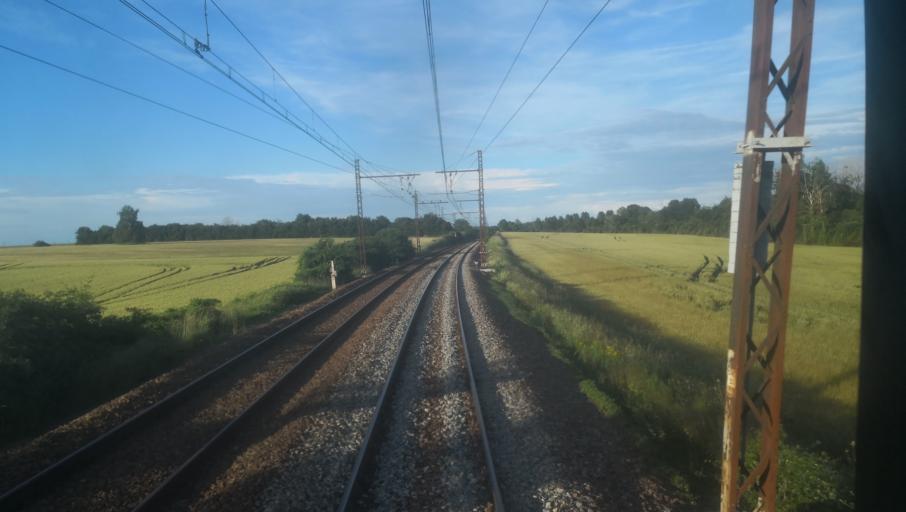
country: FR
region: Centre
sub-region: Departement de l'Indre
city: Neuvy-Pailloux
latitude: 46.8908
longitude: 1.8769
